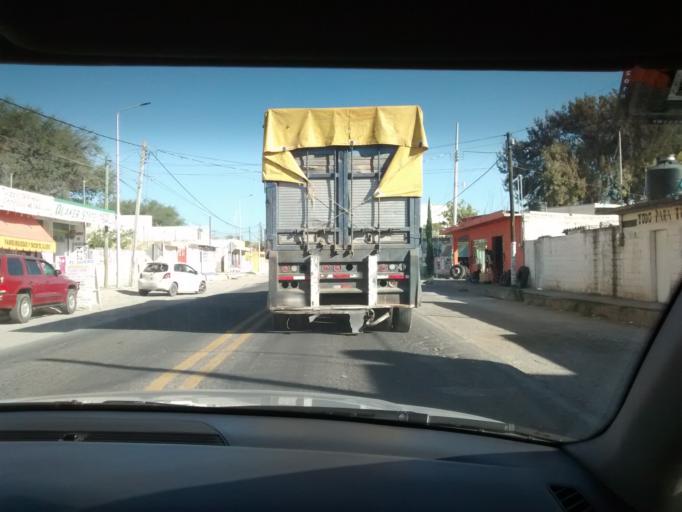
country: MX
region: Puebla
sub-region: Tepanco de Lopez
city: San Andres Cacaloapan
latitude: 18.5568
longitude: -97.5636
